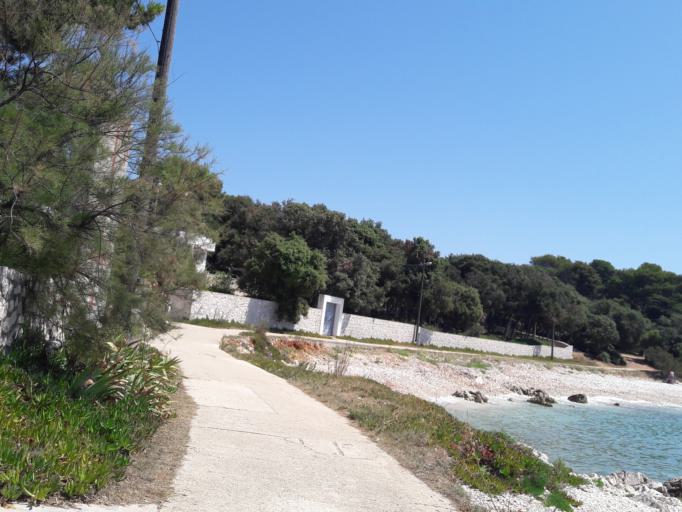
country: HR
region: Licko-Senjska
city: Novalja
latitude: 44.3701
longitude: 14.6936
